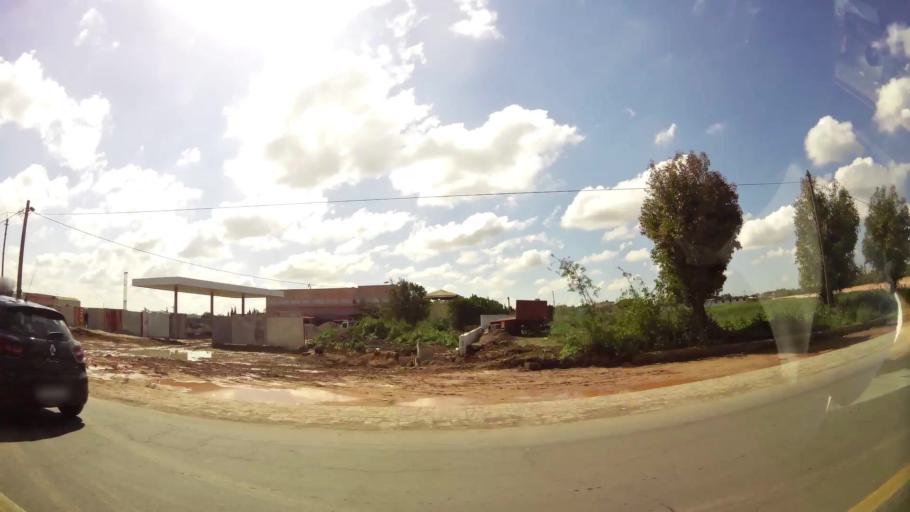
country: MA
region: Grand Casablanca
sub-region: Mediouna
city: Mediouna
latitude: 33.4395
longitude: -7.5205
